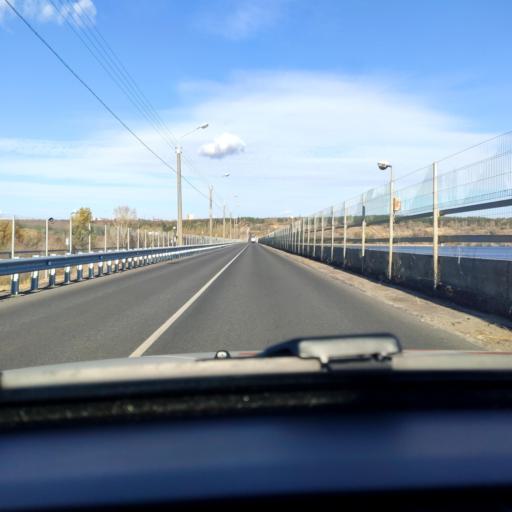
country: RU
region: Voronezj
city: Shilovo
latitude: 51.5444
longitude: 39.1369
